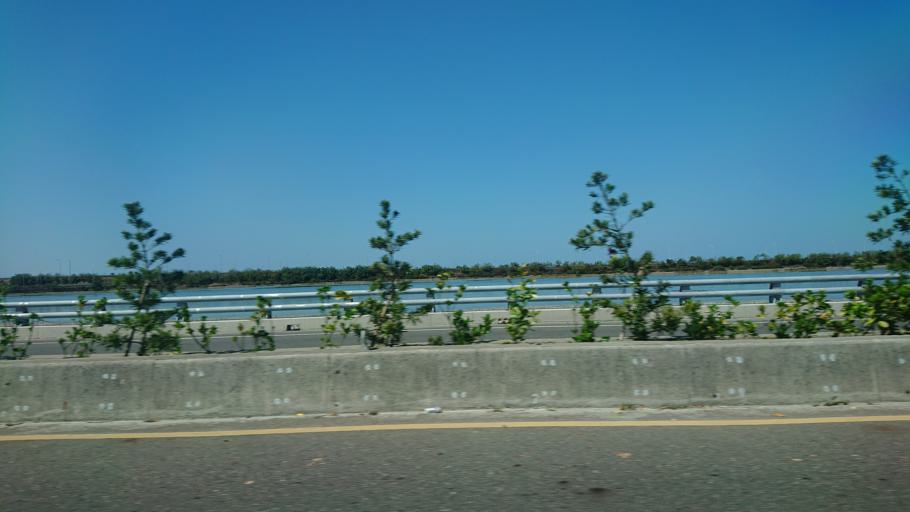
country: TW
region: Taiwan
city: Xinying
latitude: 23.2809
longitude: 120.1321
